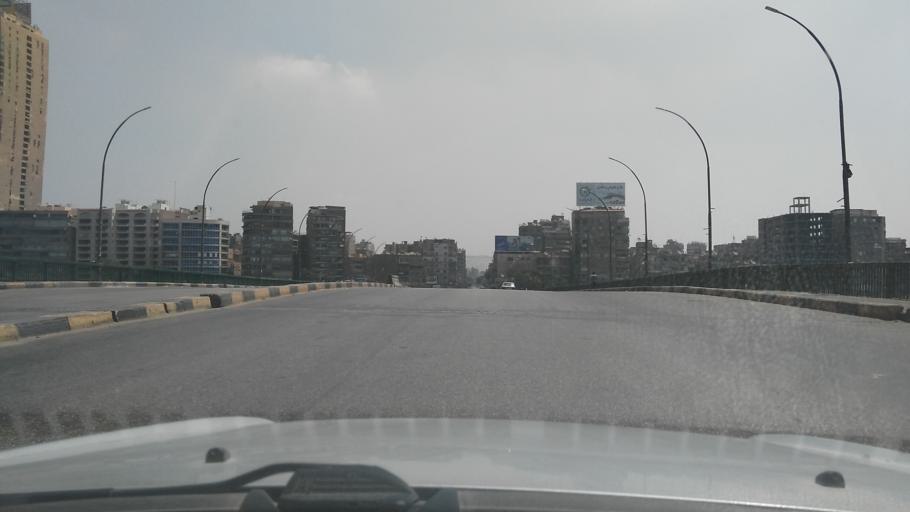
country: EG
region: Al Jizah
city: Al Jizah
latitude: 30.0160
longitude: 31.2191
